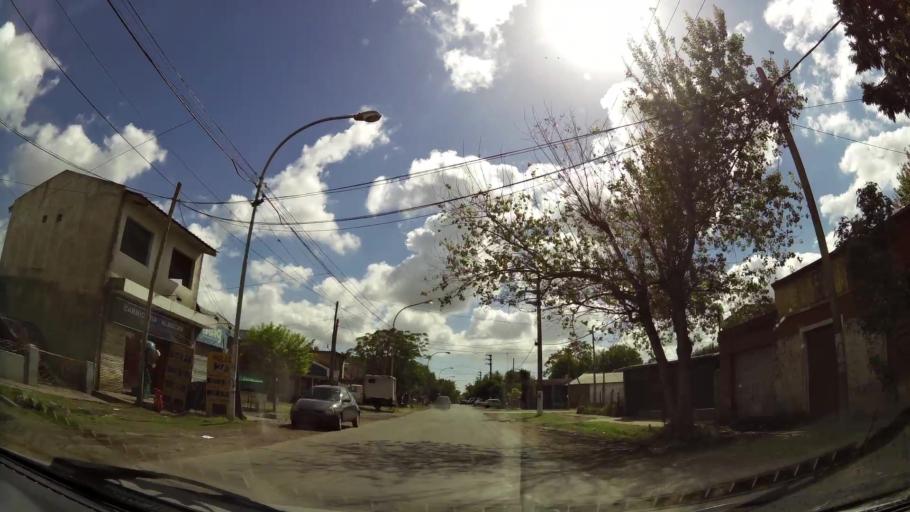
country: AR
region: Buenos Aires
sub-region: Partido de Quilmes
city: Quilmes
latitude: -34.8294
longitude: -58.1738
